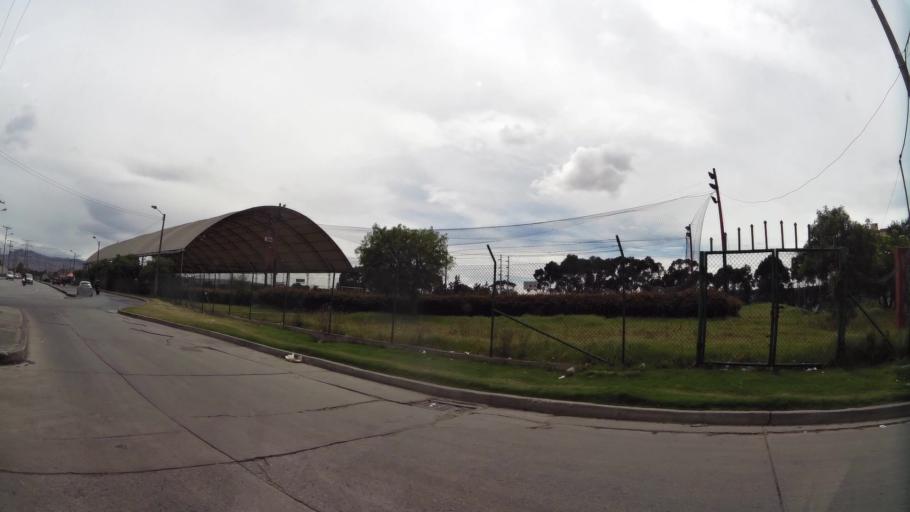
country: CO
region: Bogota D.C.
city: Bogota
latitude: 4.6318
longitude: -74.1247
